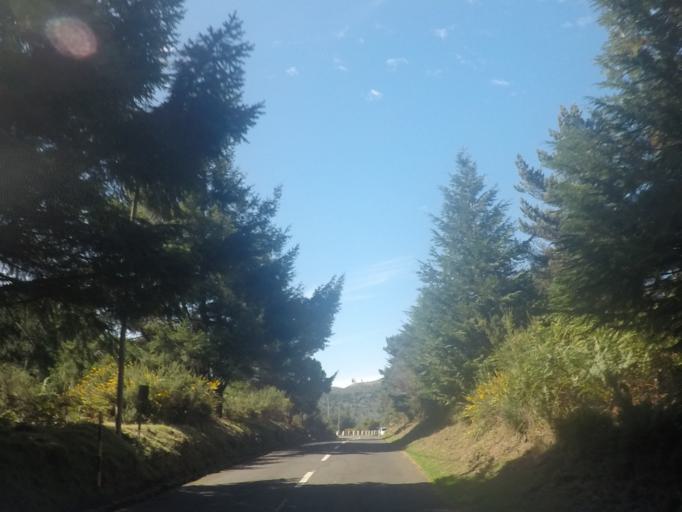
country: PT
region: Madeira
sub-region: Funchal
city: Nossa Senhora do Monte
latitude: 32.7124
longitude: -16.8901
